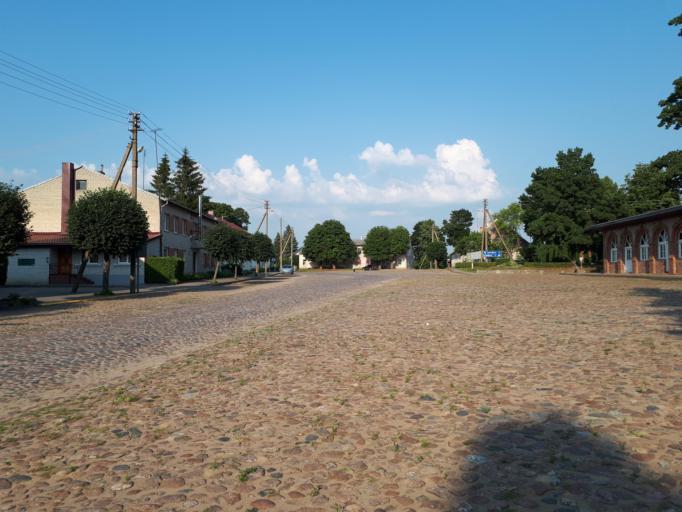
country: LT
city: Zemaiciu Naumiestis
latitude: 55.2867
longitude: 21.8161
